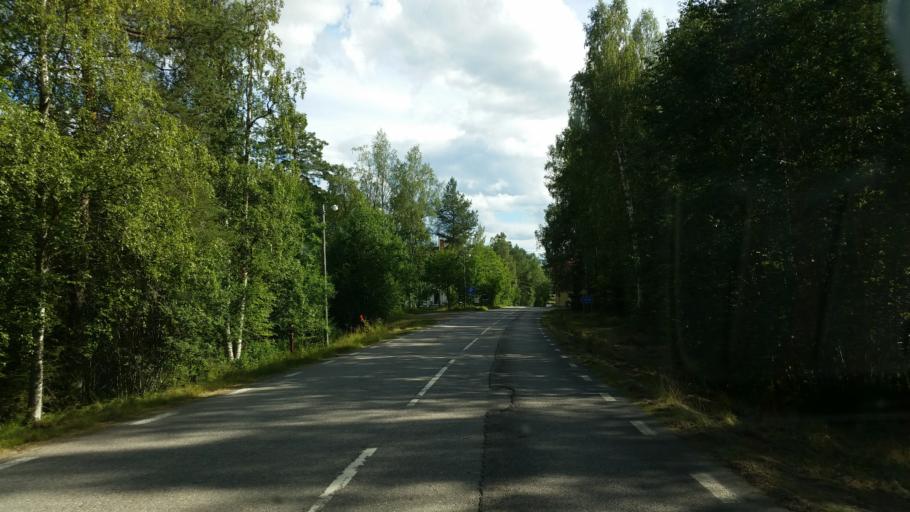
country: SE
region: Gaevleborg
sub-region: Hudiksvalls Kommun
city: Delsbo
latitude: 61.9736
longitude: 16.4658
